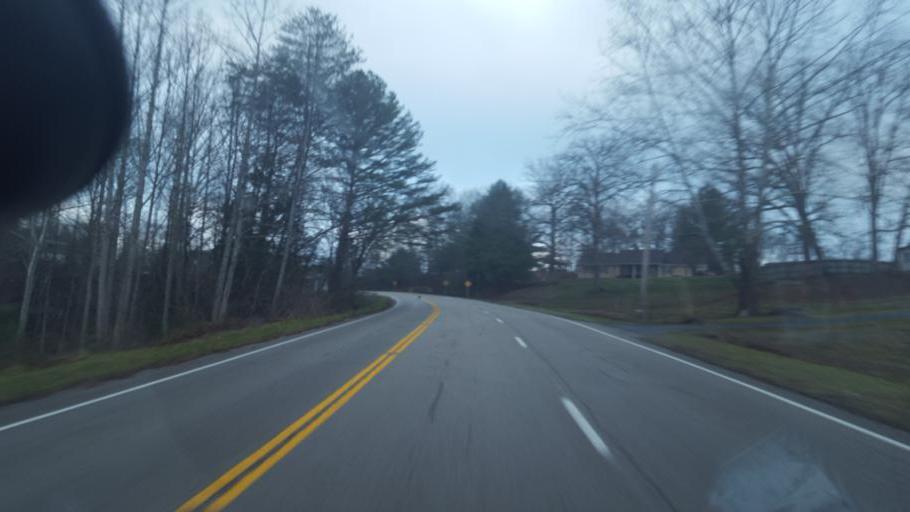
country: US
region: Kentucky
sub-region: Rockcastle County
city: Mount Vernon
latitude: 37.3026
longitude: -84.2253
